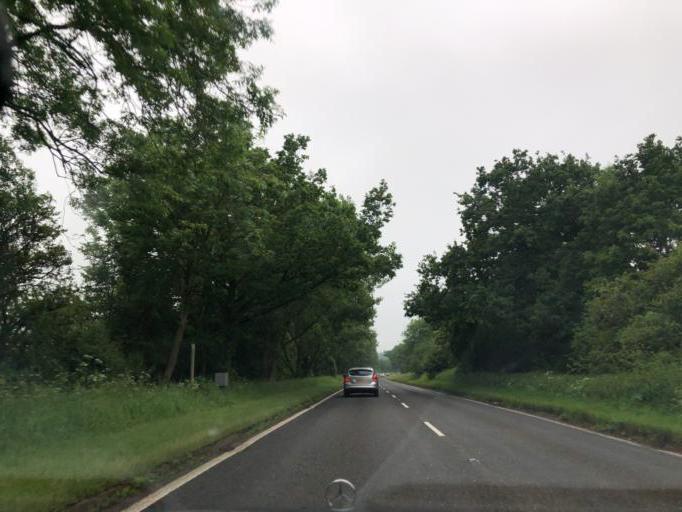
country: GB
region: England
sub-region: Warwickshire
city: Wellesbourne Mountford
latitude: 52.2253
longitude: -1.5288
